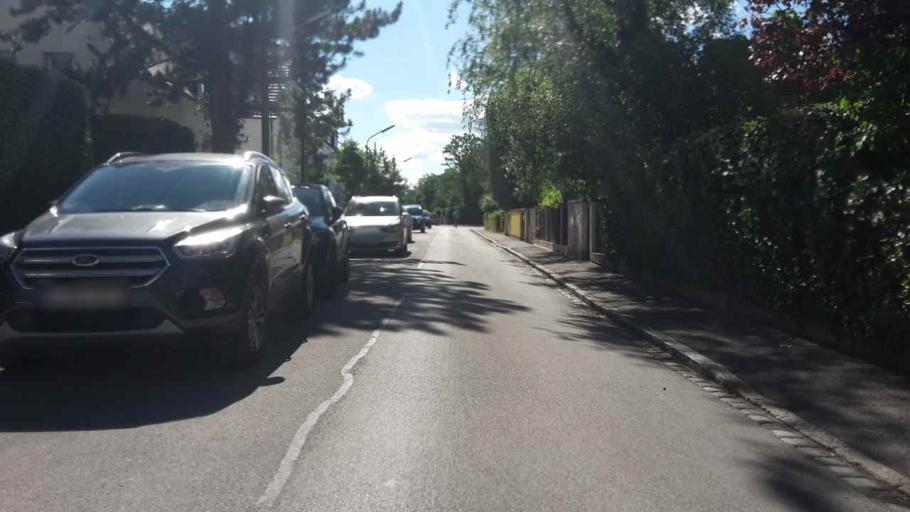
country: DE
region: Bavaria
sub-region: Upper Bavaria
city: Pasing
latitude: 48.1673
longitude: 11.4654
